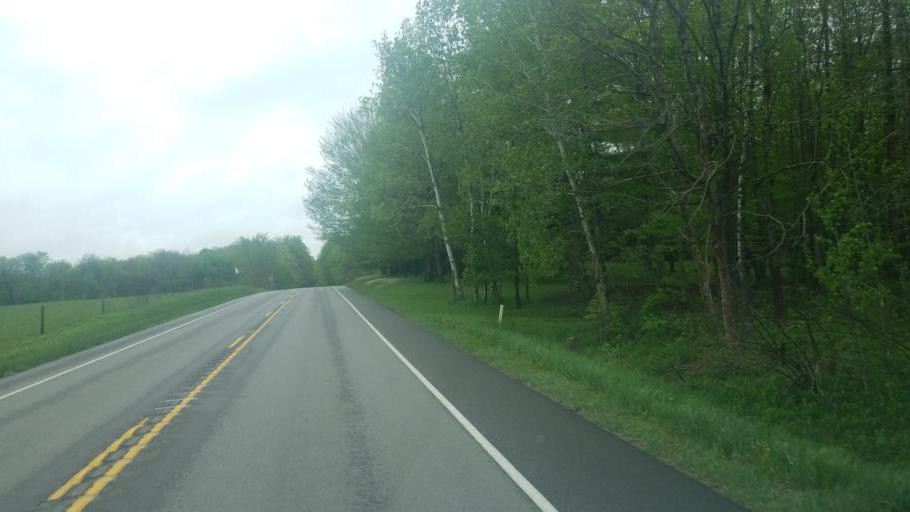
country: US
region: Pennsylvania
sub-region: Forest County
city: Marienville
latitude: 41.5177
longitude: -79.0651
